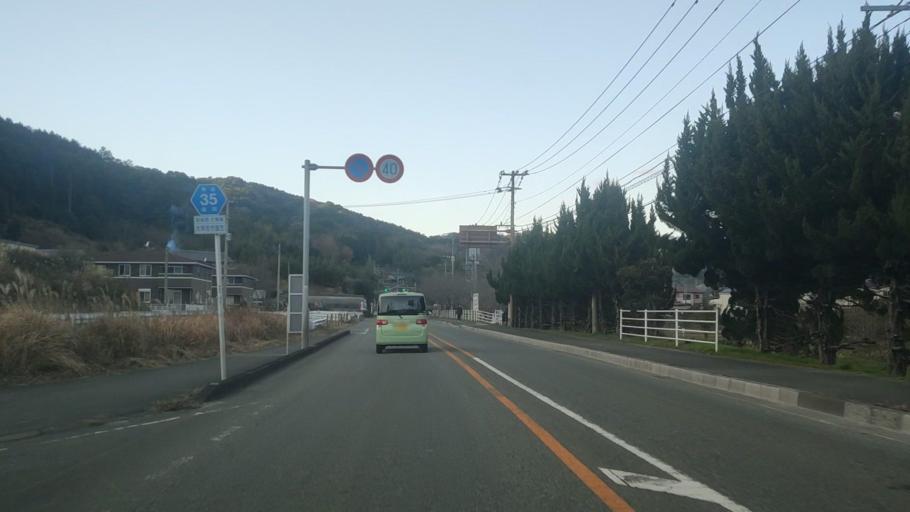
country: JP
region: Fukuoka
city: Dazaifu
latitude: 33.5381
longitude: 130.5401
